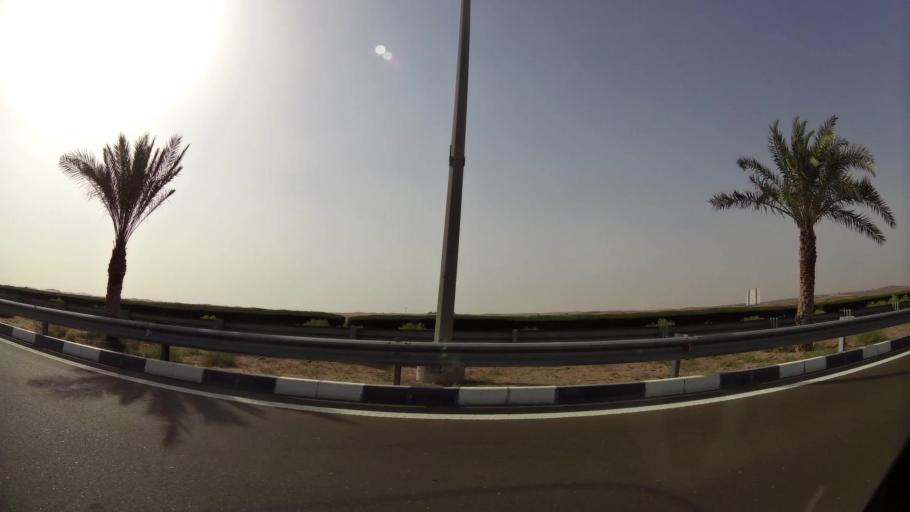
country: AE
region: Abu Dhabi
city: Al Ain
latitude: 24.2215
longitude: 55.6468
